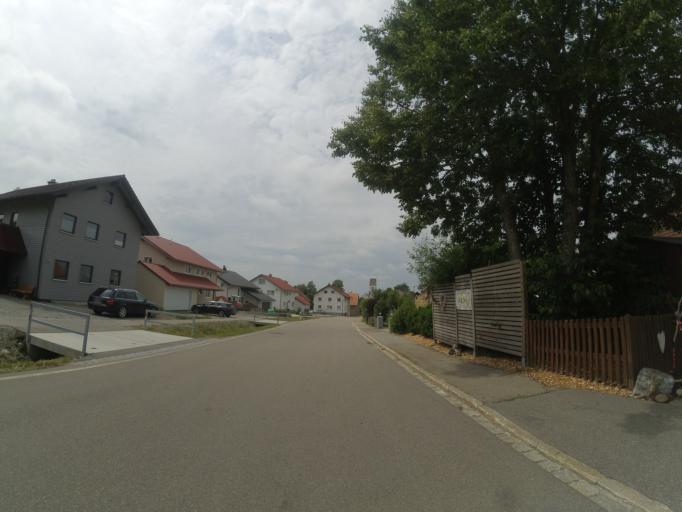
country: DE
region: Baden-Wuerttemberg
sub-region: Tuebingen Region
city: Isny im Allgau
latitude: 47.7420
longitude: 10.0151
